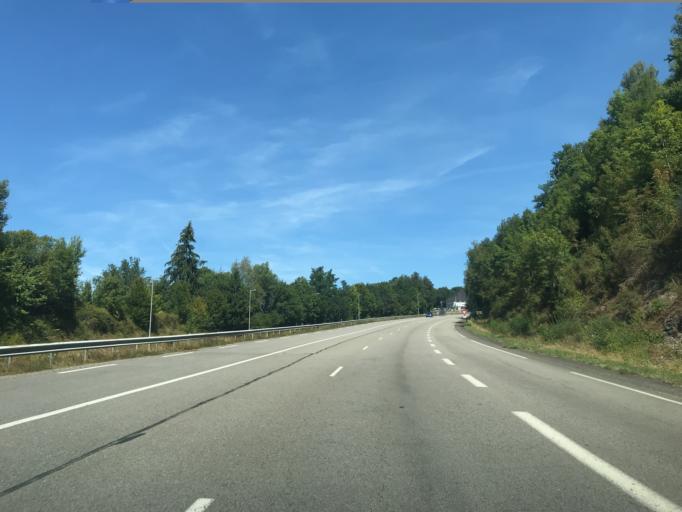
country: FR
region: Limousin
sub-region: Departement de la Correze
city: Tulle
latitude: 45.2753
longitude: 1.7888
